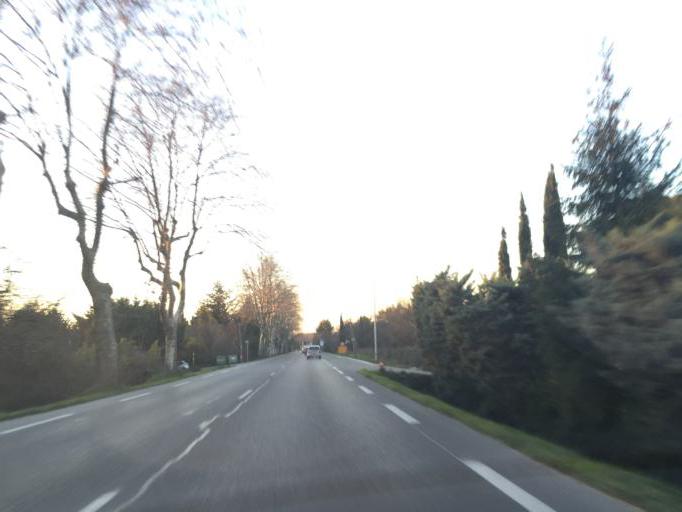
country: FR
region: Provence-Alpes-Cote d'Azur
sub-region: Departement des Bouches-du-Rhone
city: Eguilles
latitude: 43.5627
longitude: 5.4085
